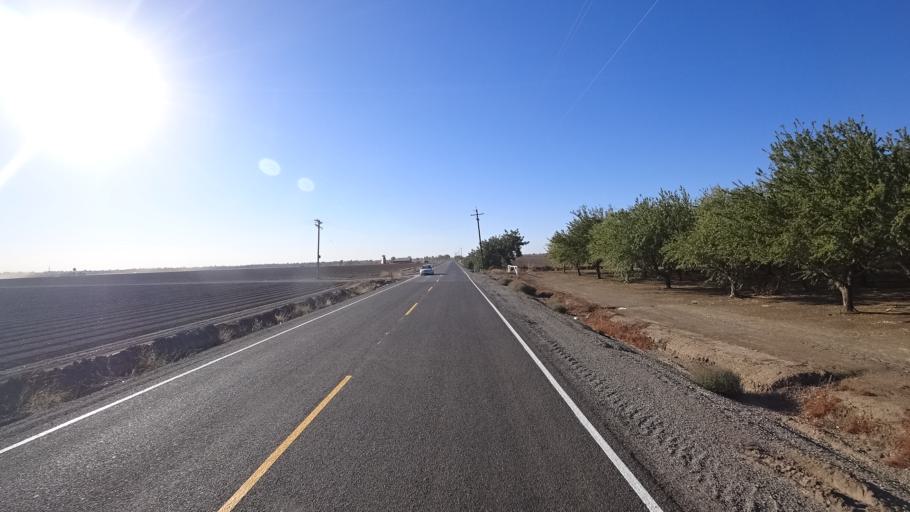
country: US
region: California
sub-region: Yolo County
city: Davis
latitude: 38.5766
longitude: -121.7860
